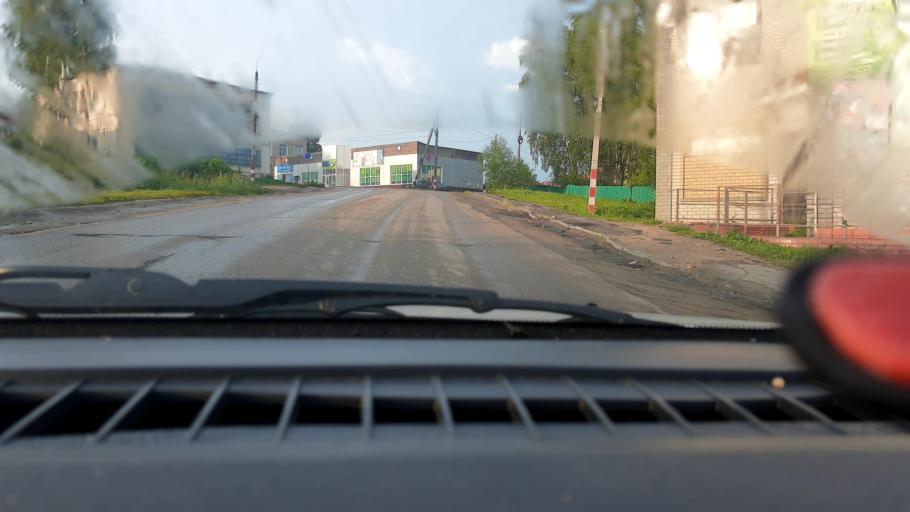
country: RU
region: Nizjnij Novgorod
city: Lukoyanov
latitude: 55.0317
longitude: 44.4944
